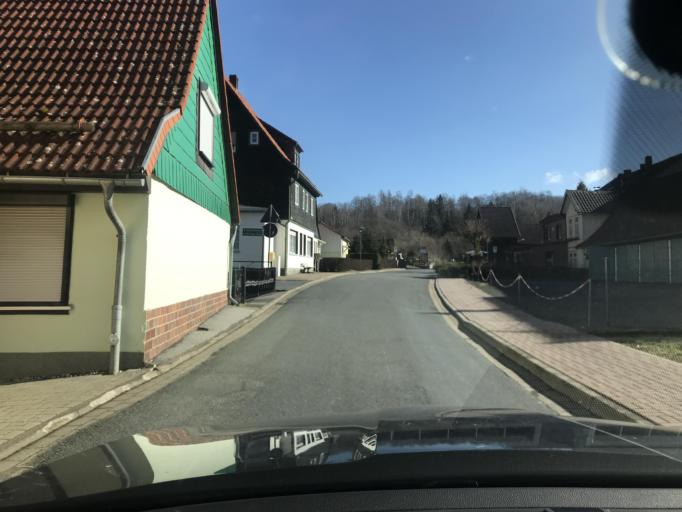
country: DE
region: Saxony-Anhalt
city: Huttenrode
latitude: 51.7263
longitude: 10.9422
